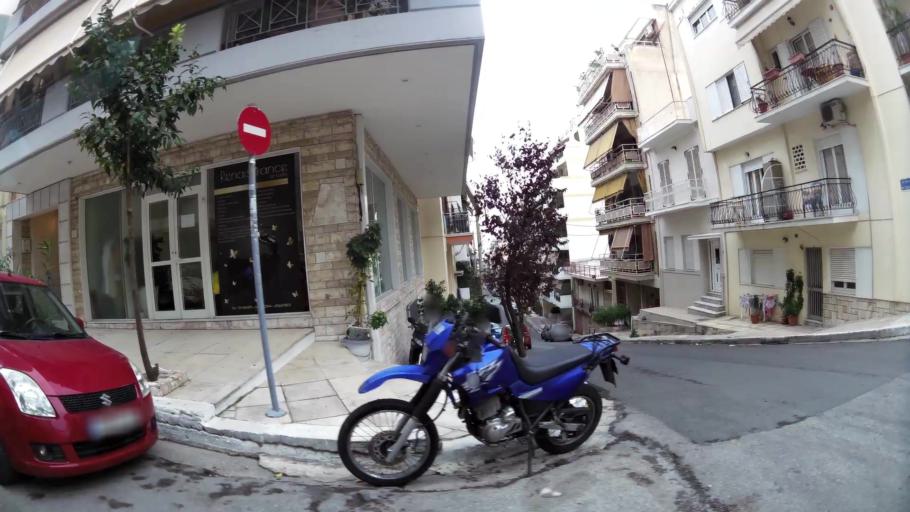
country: GR
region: Attica
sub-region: Nomos Attikis
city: Piraeus
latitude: 37.9327
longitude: 23.6327
